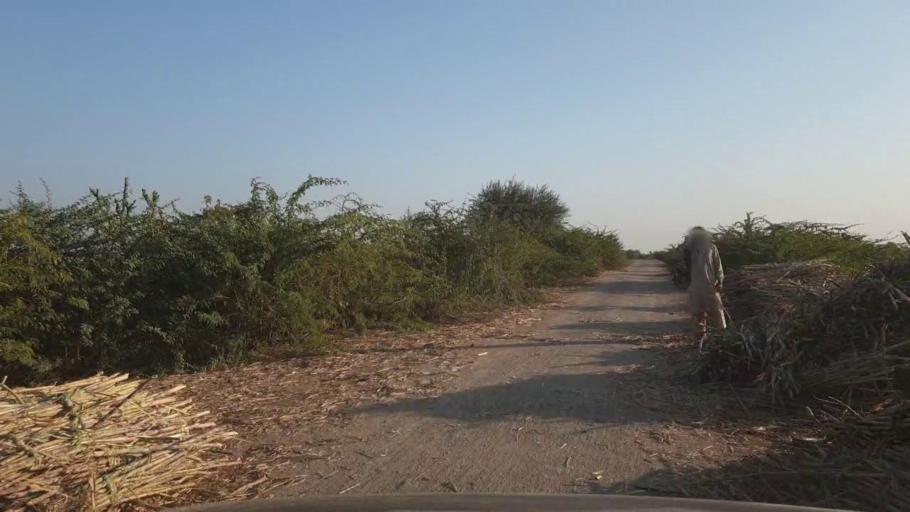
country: PK
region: Sindh
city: Digri
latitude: 25.1244
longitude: 69.2945
